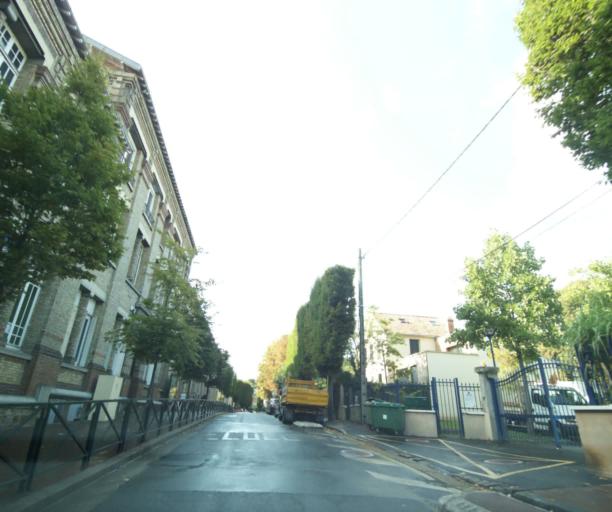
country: FR
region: Ile-de-France
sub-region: Departement des Hauts-de-Seine
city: Clamart
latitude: 48.8065
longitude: 2.2612
